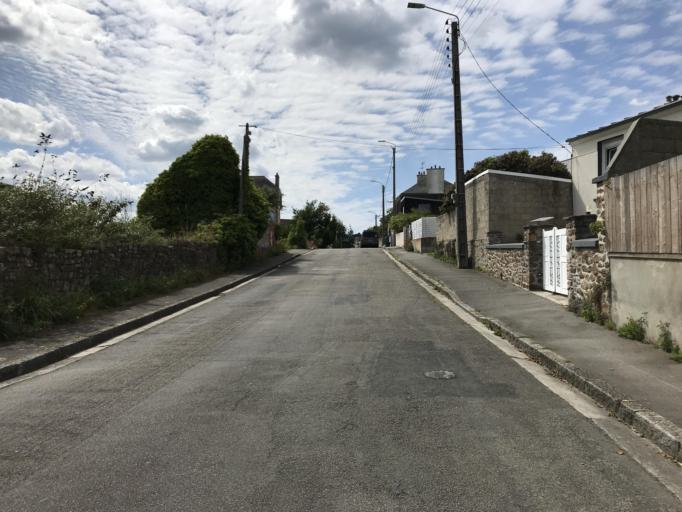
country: FR
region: Brittany
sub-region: Departement du Finistere
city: Brest
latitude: 48.3971
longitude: -4.4474
